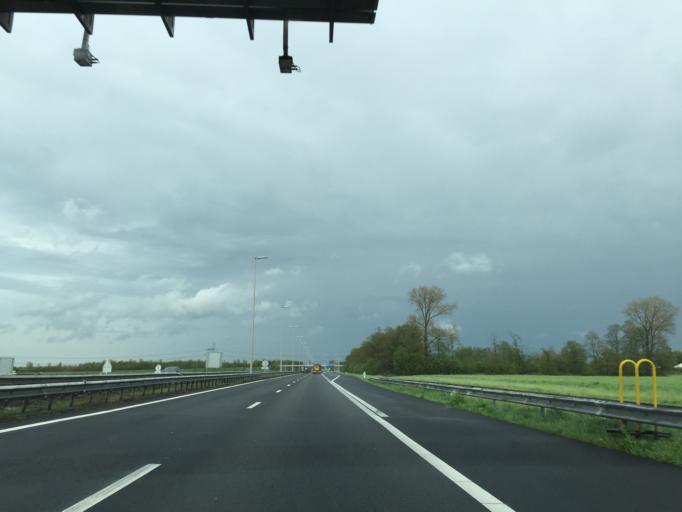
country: NL
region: Gelderland
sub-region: Gemeente Hattem
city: Hattem
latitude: 52.4786
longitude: 6.0085
